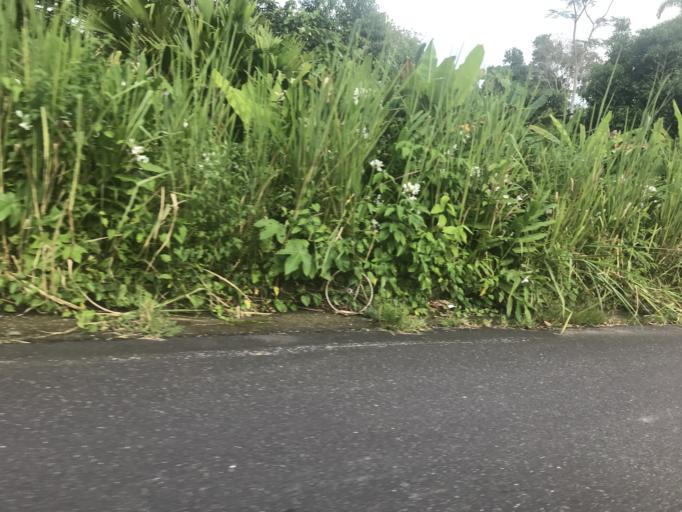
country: EC
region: Napo
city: Tena
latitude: -1.0462
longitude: -77.8097
